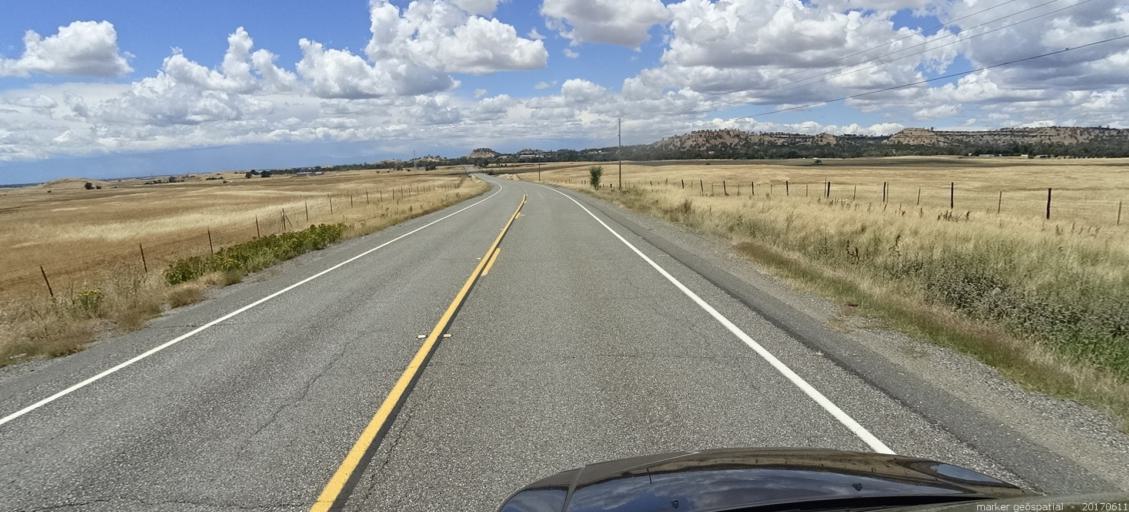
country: US
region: California
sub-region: Butte County
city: Paradise
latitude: 39.6473
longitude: -121.6207
